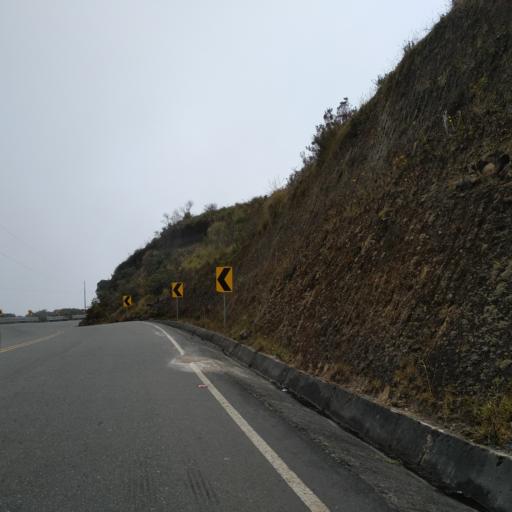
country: EC
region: Cotopaxi
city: La Mana
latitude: -0.9884
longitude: -78.9665
